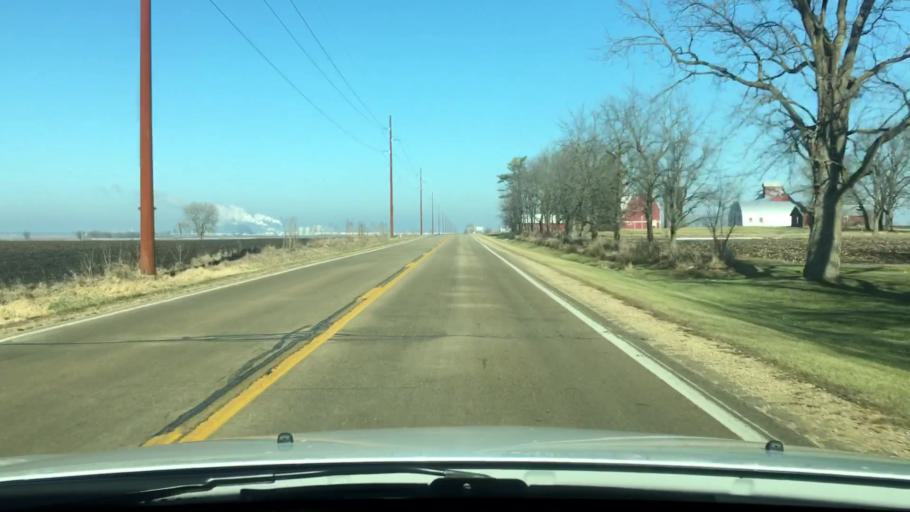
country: US
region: Illinois
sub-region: Ogle County
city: Rochelle
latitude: 41.8571
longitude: -89.0248
